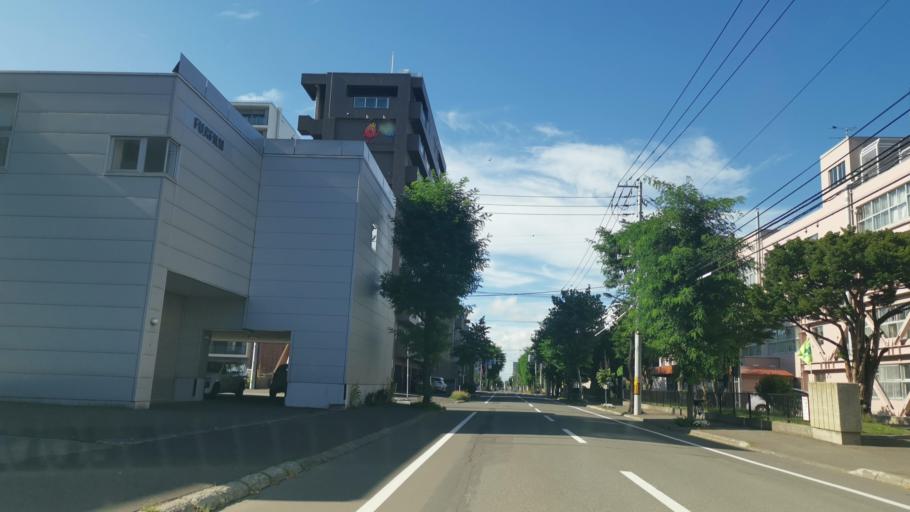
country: JP
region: Hokkaido
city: Sapporo
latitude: 43.0821
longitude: 141.3483
